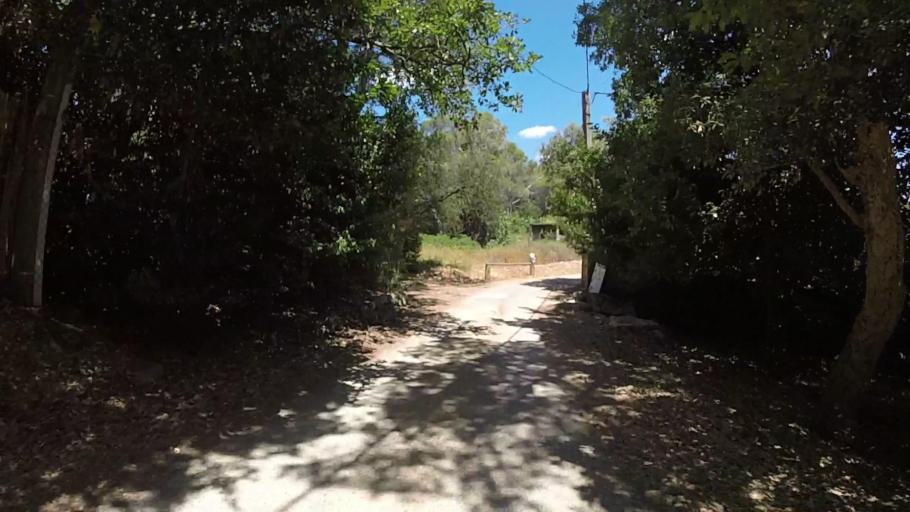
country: FR
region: Provence-Alpes-Cote d'Azur
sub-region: Departement des Alpes-Maritimes
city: Vallauris
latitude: 43.5961
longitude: 7.0433
